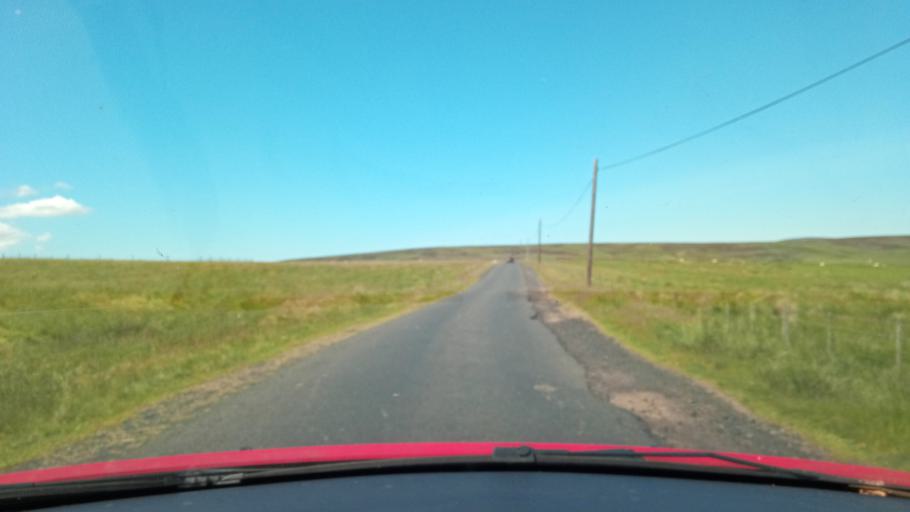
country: GB
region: Scotland
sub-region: The Scottish Borders
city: Duns
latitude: 55.8247
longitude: -2.5148
